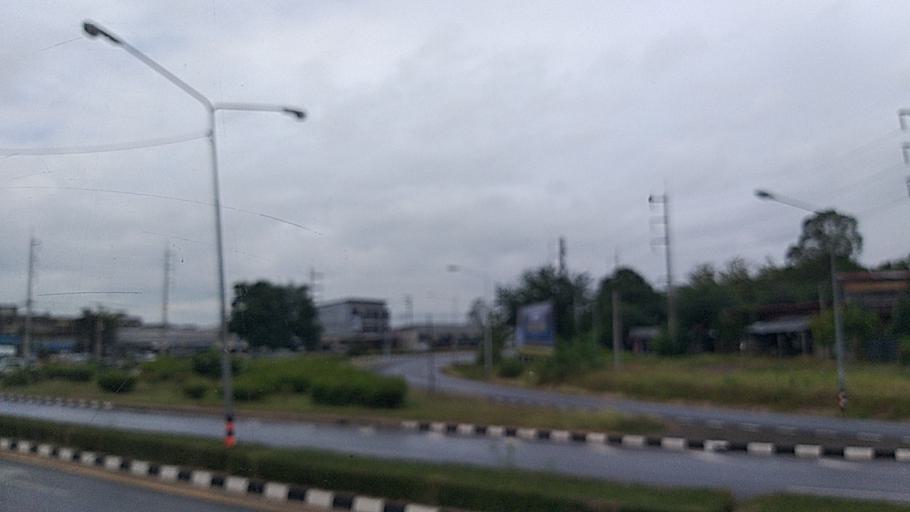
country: TH
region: Maha Sarakham
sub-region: Amphoe Borabue
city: Borabue
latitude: 16.0448
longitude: 103.1240
